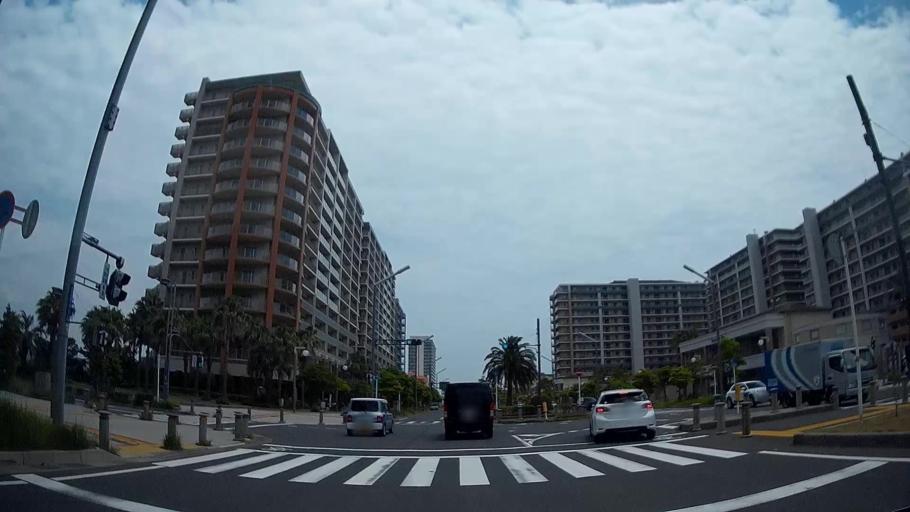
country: JP
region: Tokyo
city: Urayasu
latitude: 35.6407
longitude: 139.9273
